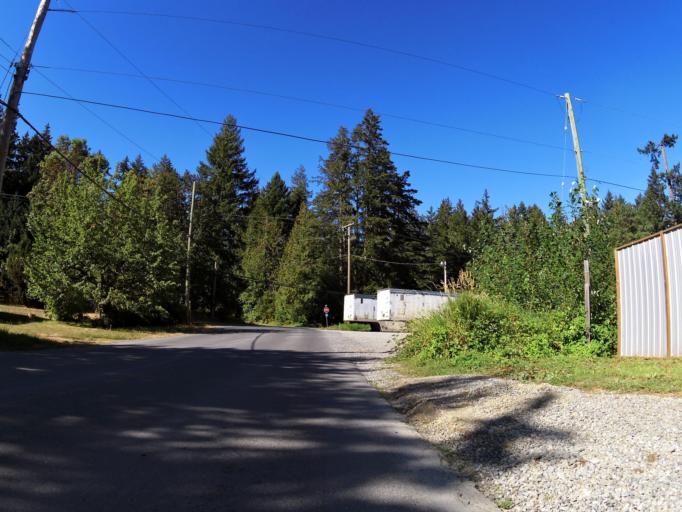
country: CA
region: British Columbia
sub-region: Cowichan Valley Regional District
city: Ladysmith
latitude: 49.0422
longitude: -123.8512
